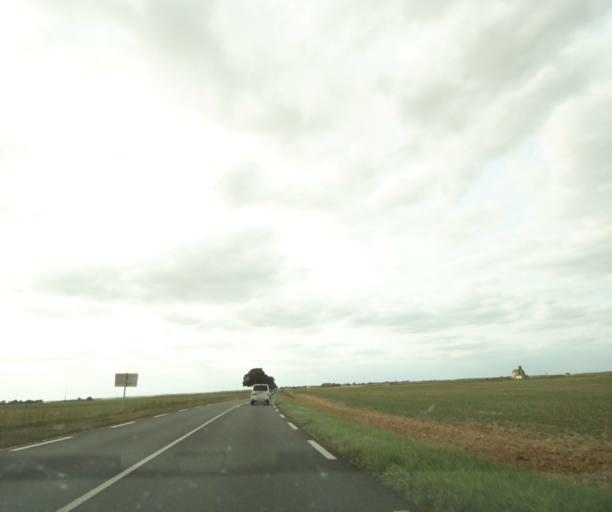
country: FR
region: Centre
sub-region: Departement d'Indre-et-Loire
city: Chambourg-sur-Indre
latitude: 47.1862
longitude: 0.9426
